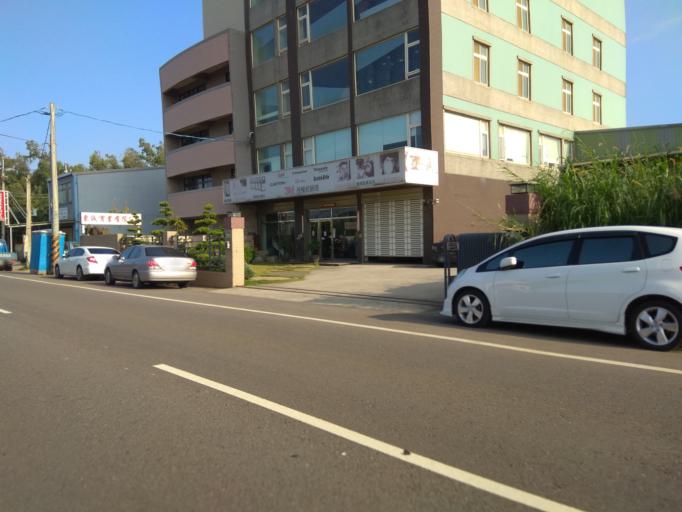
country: TW
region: Taiwan
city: Taoyuan City
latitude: 24.9654
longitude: 121.1417
